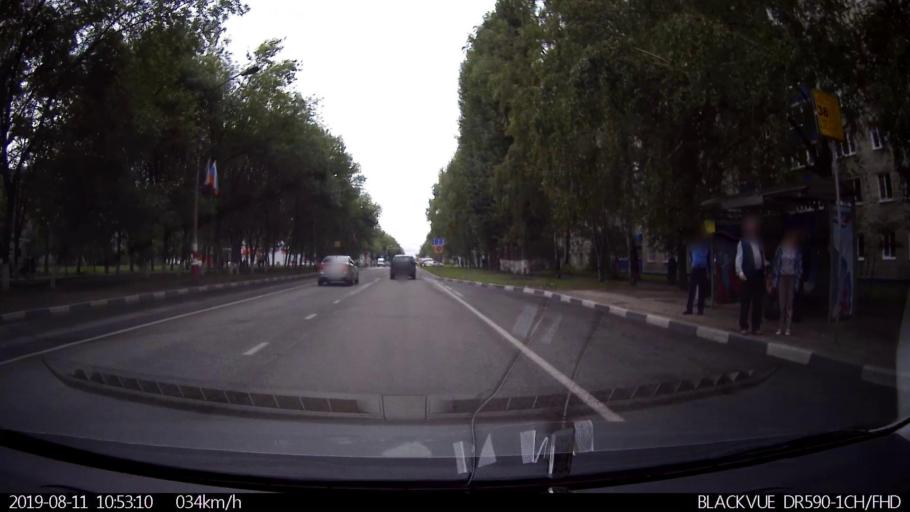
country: RU
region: Ulyanovsk
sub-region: Ulyanovskiy Rayon
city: Ulyanovsk
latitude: 54.2611
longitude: 48.3343
